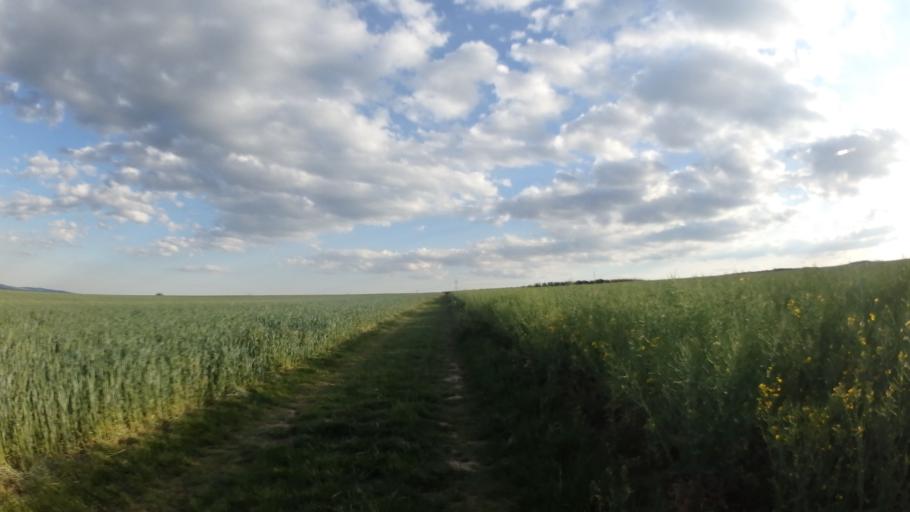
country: CZ
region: South Moravian
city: Moravany
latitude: 49.1387
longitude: 16.5913
